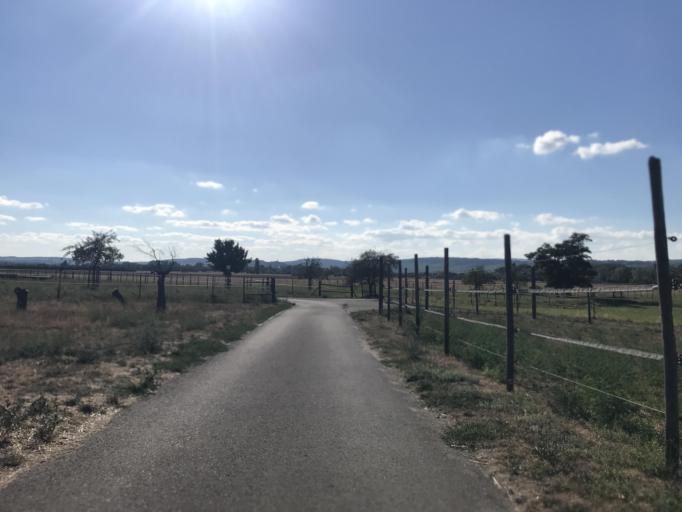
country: DE
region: Rheinland-Pfalz
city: Gau-Algesheim
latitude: 49.9762
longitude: 8.0064
